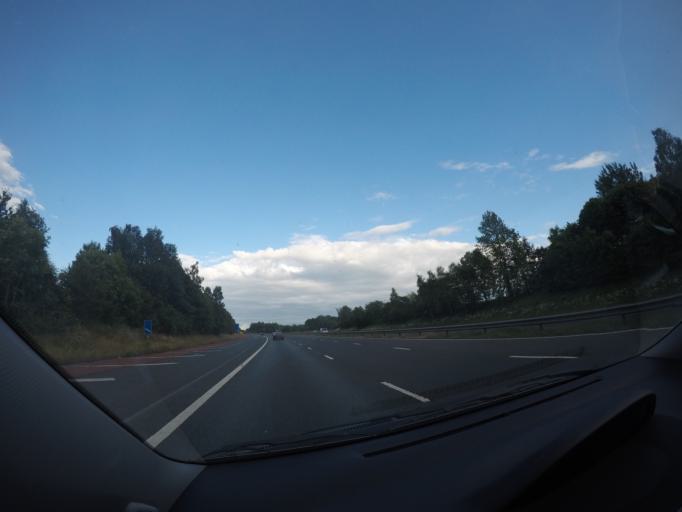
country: GB
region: England
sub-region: Cumbria
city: Carlisle
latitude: 54.9326
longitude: -2.9564
